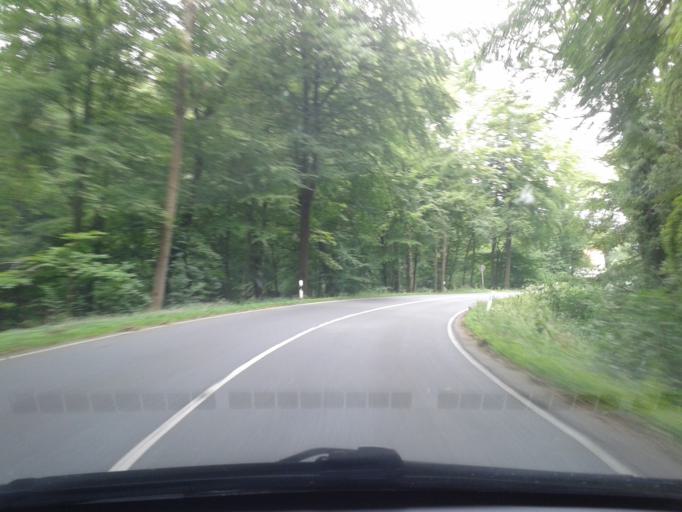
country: DE
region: North Rhine-Westphalia
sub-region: Regierungsbezirk Detmold
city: Lemgo
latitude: 52.0006
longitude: 8.9165
